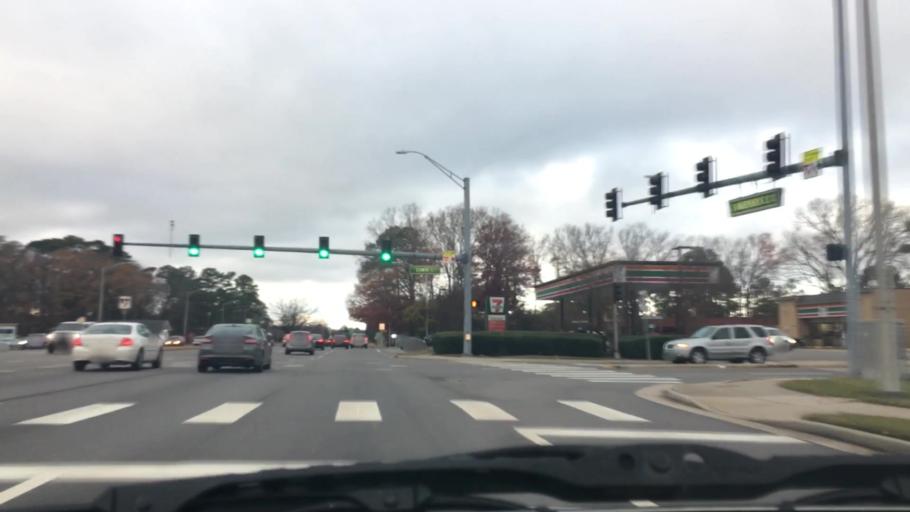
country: US
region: Virginia
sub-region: City of Chesapeake
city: Chesapeake
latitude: 36.8262
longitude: -76.1306
